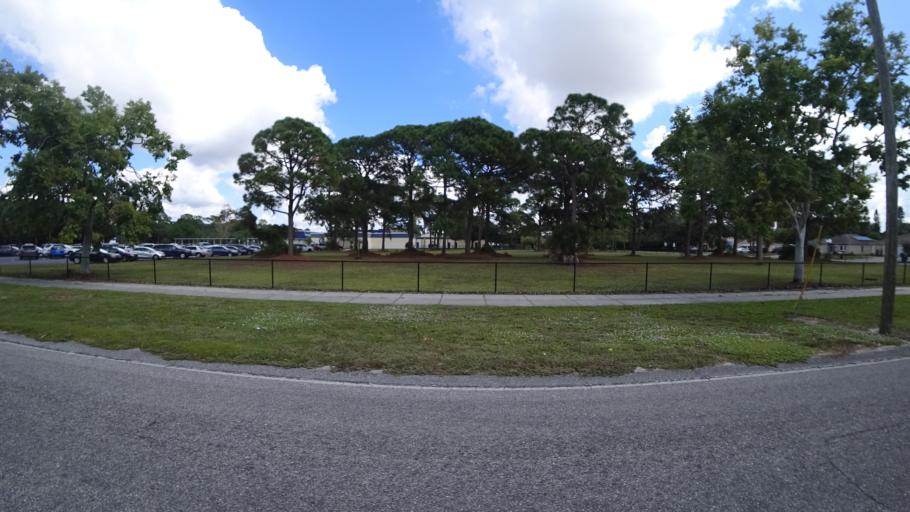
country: US
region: Florida
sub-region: Manatee County
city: Whitfield
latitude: 27.4263
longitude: -82.5550
